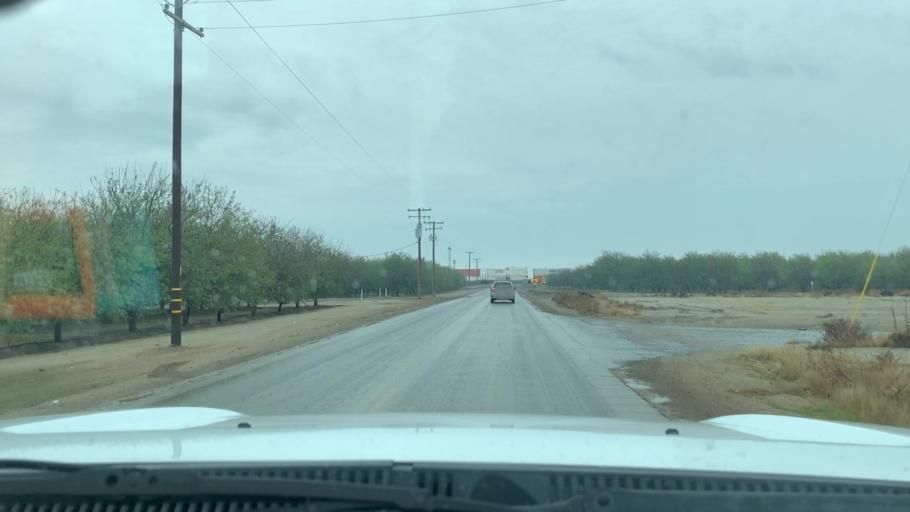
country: US
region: California
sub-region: Kern County
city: Delano
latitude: 35.7612
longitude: -119.3489
